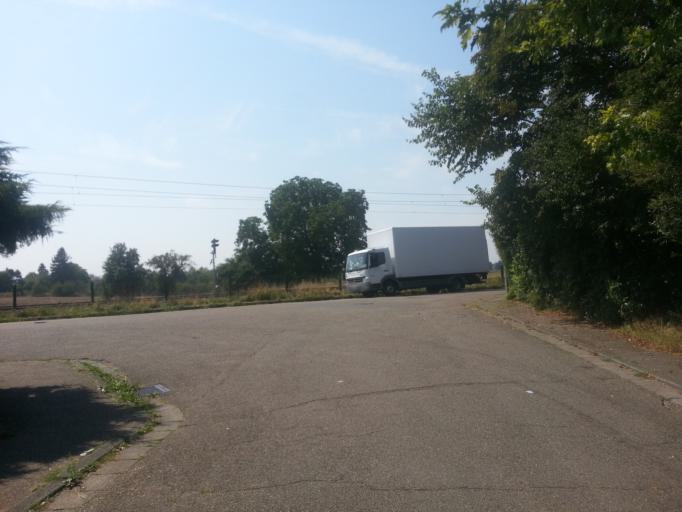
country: DE
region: Baden-Wuerttemberg
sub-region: Karlsruhe Region
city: Edingen-Neckarhausen
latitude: 49.4483
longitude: 8.6025
